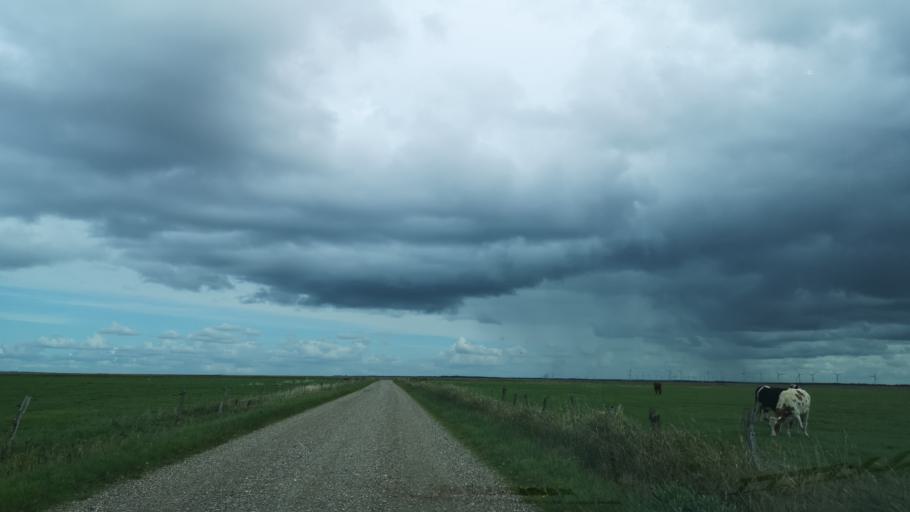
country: DK
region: Central Jutland
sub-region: Ringkobing-Skjern Kommune
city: Hvide Sande
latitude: 55.8678
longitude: 8.2251
